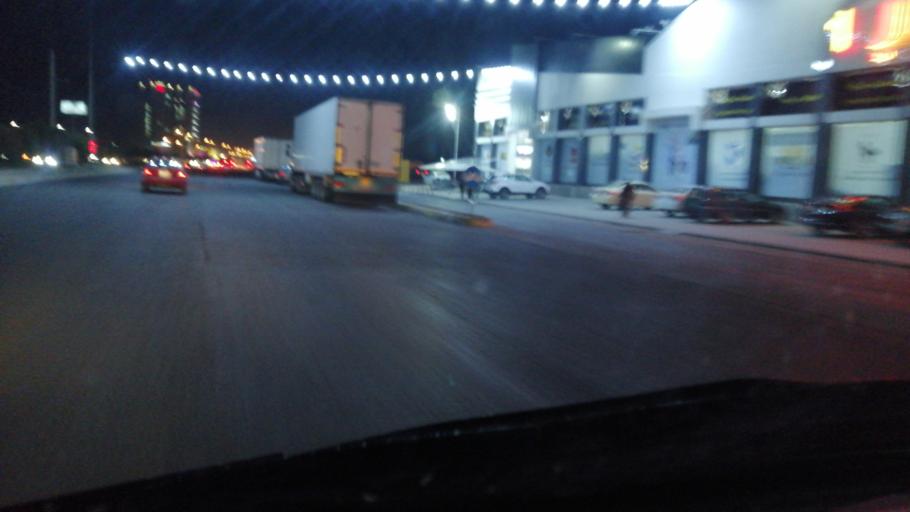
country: IQ
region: Arbil
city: Erbil
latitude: 36.1571
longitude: 43.9876
